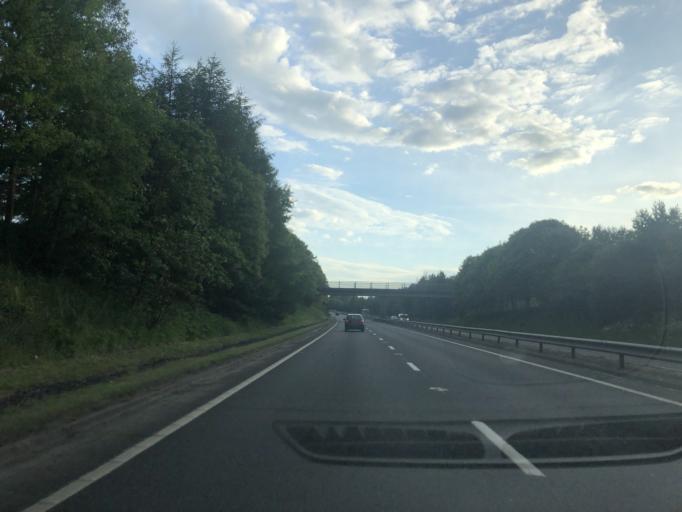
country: GB
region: Scotland
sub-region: Fife
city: Cardenden
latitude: 56.1324
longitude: -3.2432
